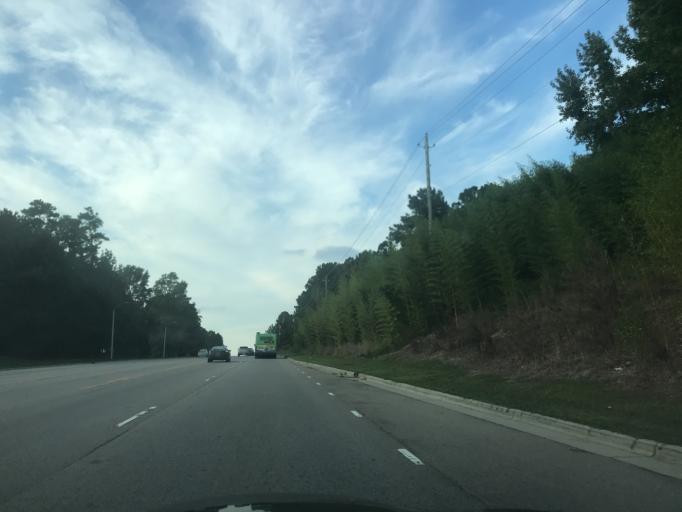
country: US
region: North Carolina
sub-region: Wake County
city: Green Level
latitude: 35.7962
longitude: -78.8705
